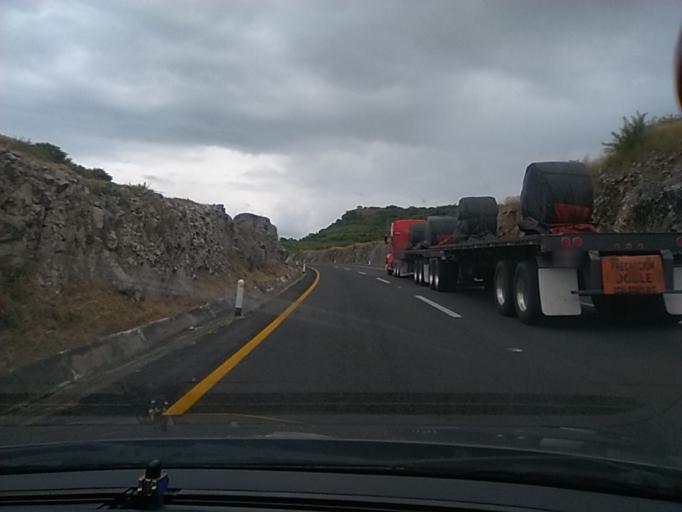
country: MX
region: Jalisco
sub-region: Zapotlan del Rey
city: Zapotlan del Rey
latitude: 20.4768
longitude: -102.9343
